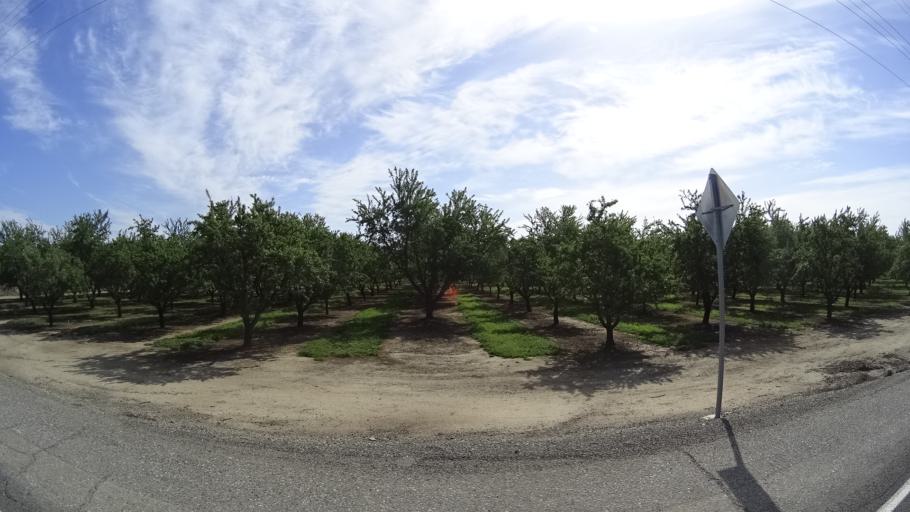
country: US
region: California
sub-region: Glenn County
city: Hamilton City
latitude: 39.6322
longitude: -122.0068
